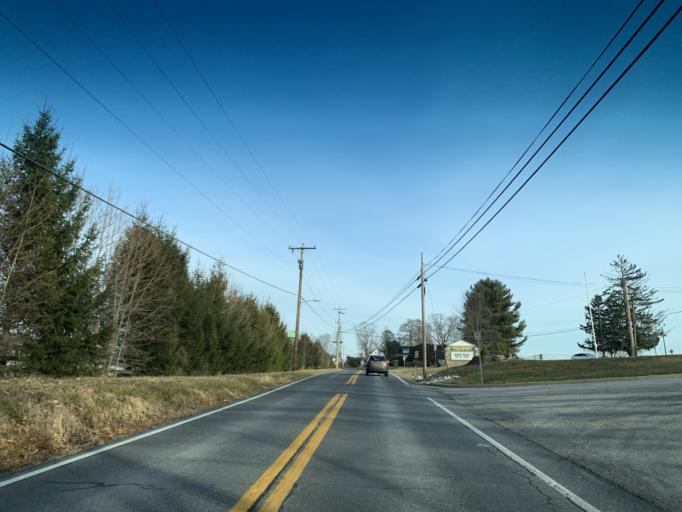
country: US
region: Maryland
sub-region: Carroll County
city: Hampstead
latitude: 39.6016
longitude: -76.7780
